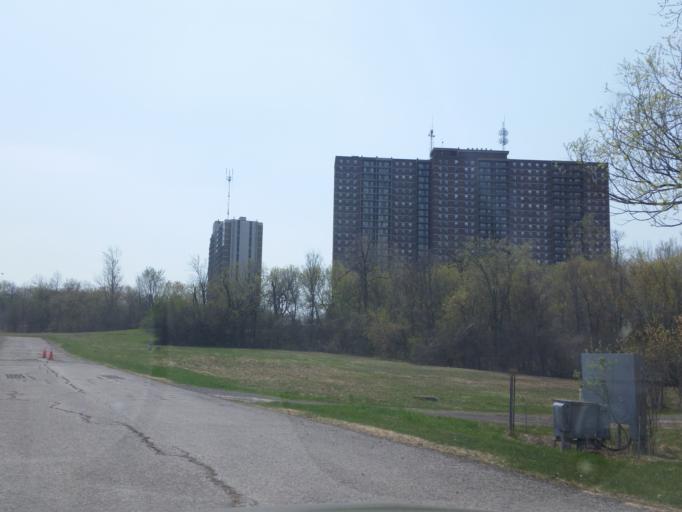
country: CA
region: Quebec
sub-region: Outaouais
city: Gatineau
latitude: 45.4492
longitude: -75.6237
